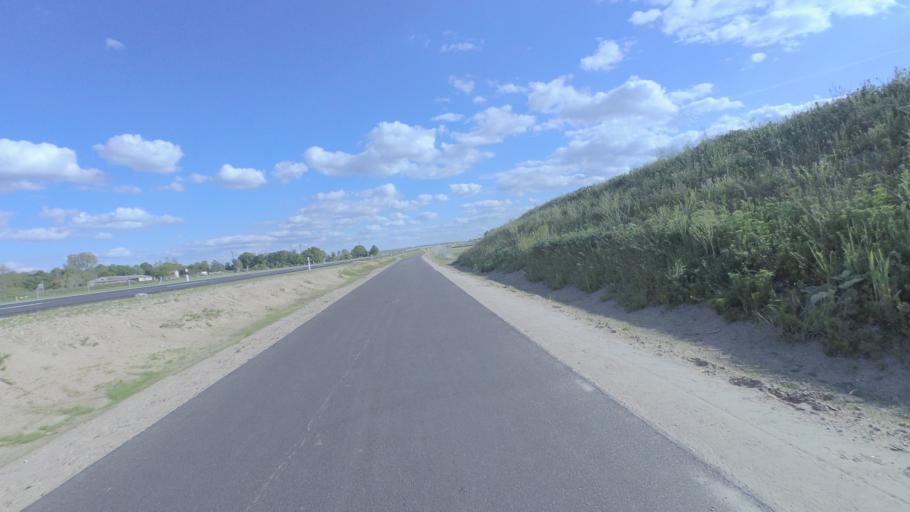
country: DE
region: Brandenburg
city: Stahnsdorf
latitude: 52.3756
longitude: 13.2367
